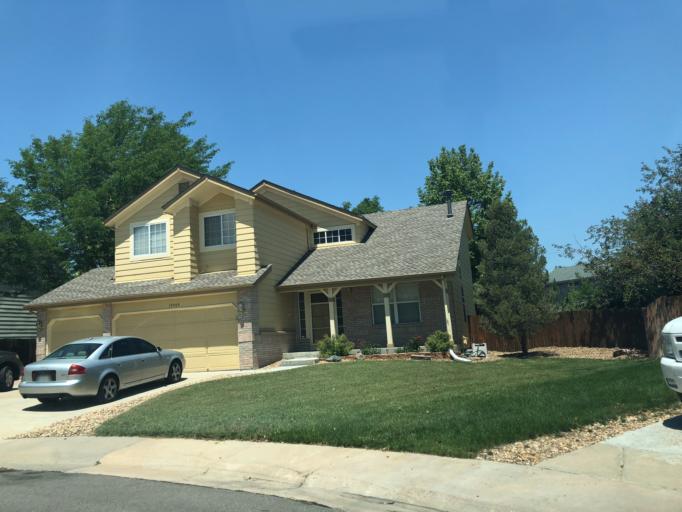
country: US
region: Colorado
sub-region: Arapahoe County
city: Dove Valley
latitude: 39.6229
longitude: -104.7548
